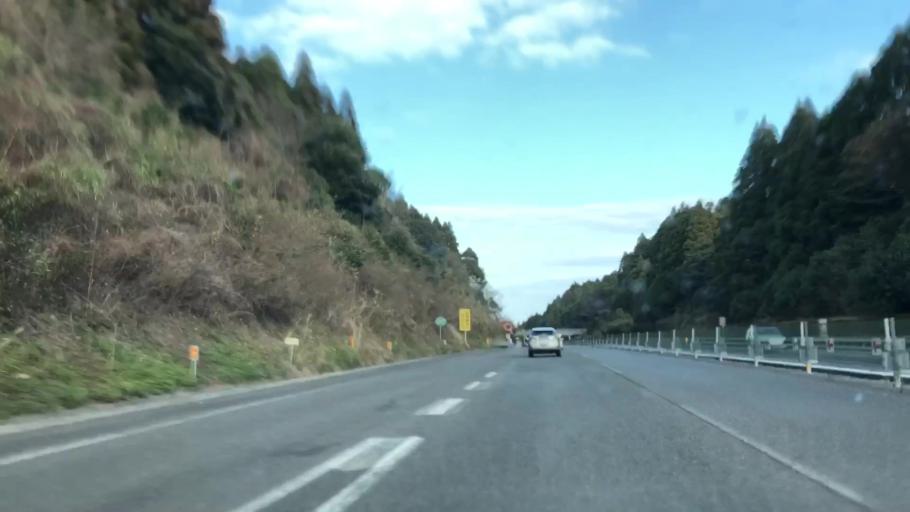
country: JP
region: Miyazaki
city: Miyazaki-shi
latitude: 31.8509
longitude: 131.3642
